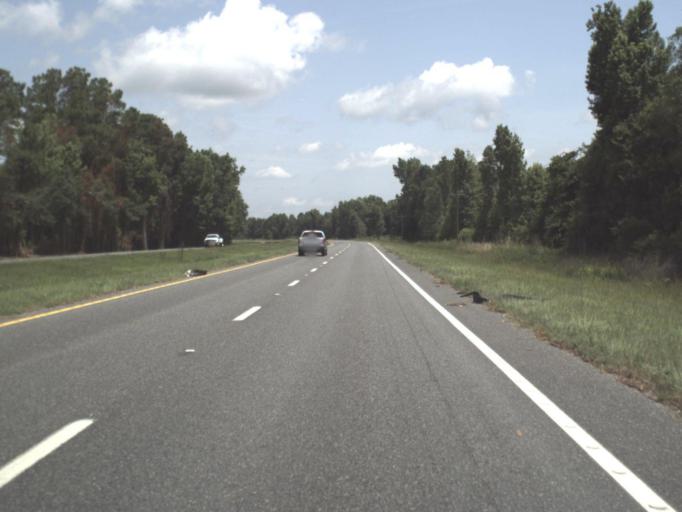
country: US
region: Florida
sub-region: Taylor County
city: Perry
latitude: 29.9417
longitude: -83.4492
